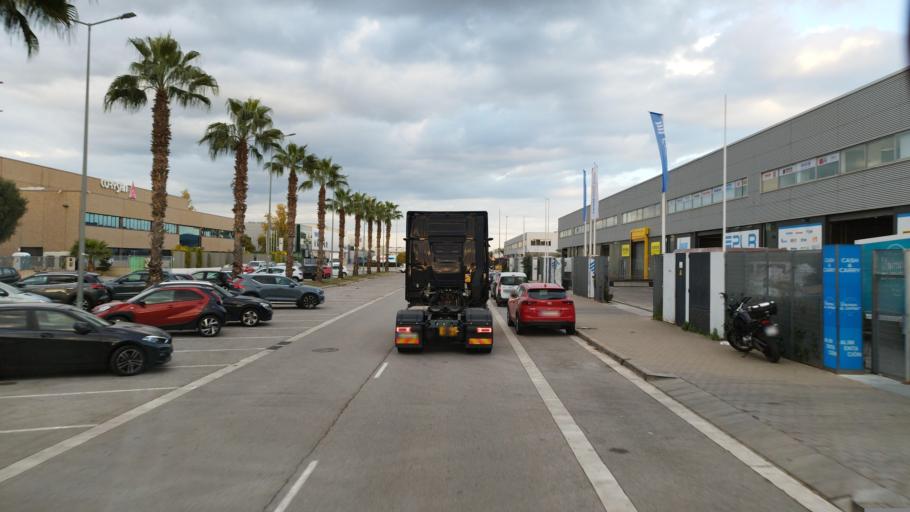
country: ES
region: Catalonia
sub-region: Provincia de Barcelona
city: Viladecans
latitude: 41.3188
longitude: 2.0322
